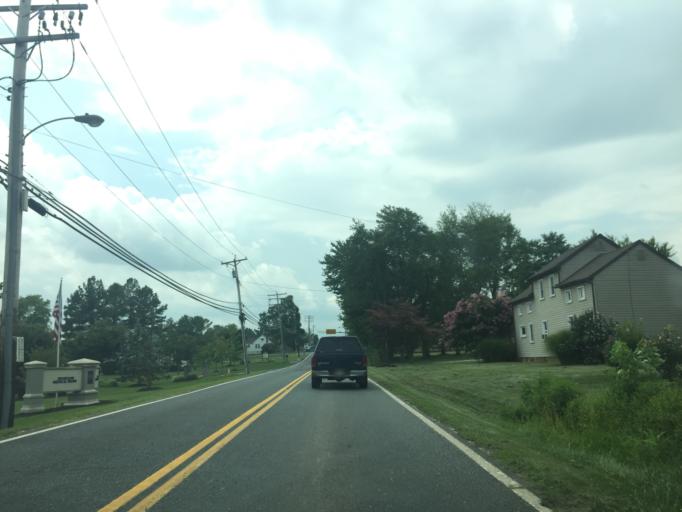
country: US
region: Maryland
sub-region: Baltimore County
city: White Marsh
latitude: 39.3866
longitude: -76.4300
